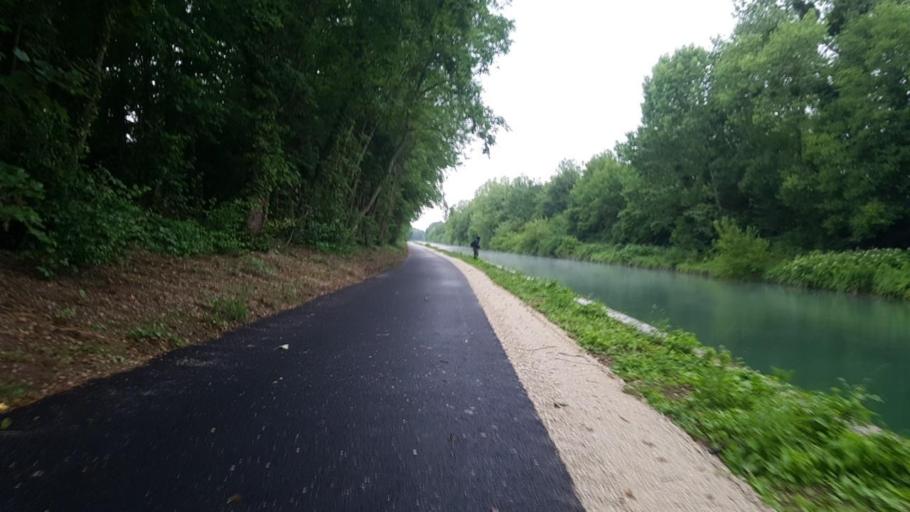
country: FR
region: Champagne-Ardenne
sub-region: Departement de la Marne
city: Sarry
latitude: 48.8639
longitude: 4.4725
